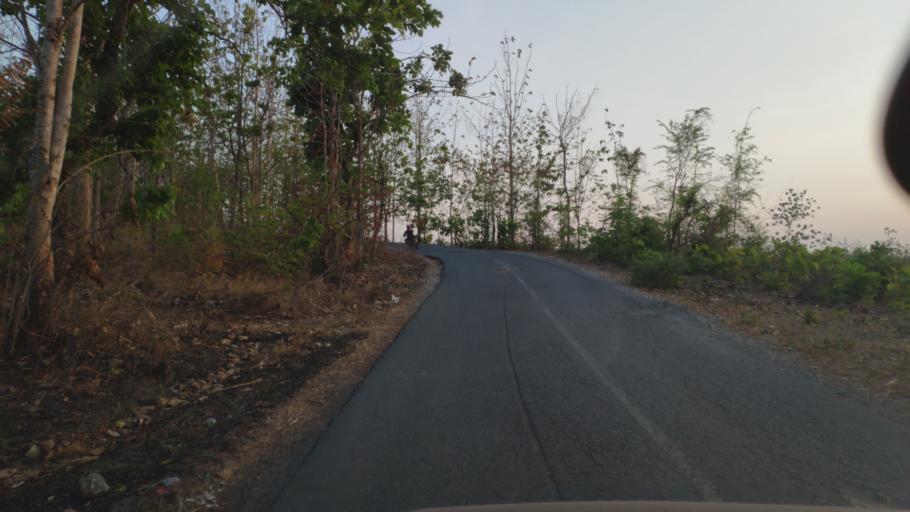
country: ID
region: Central Java
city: Semanggi
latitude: -7.0531
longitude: 111.4107
